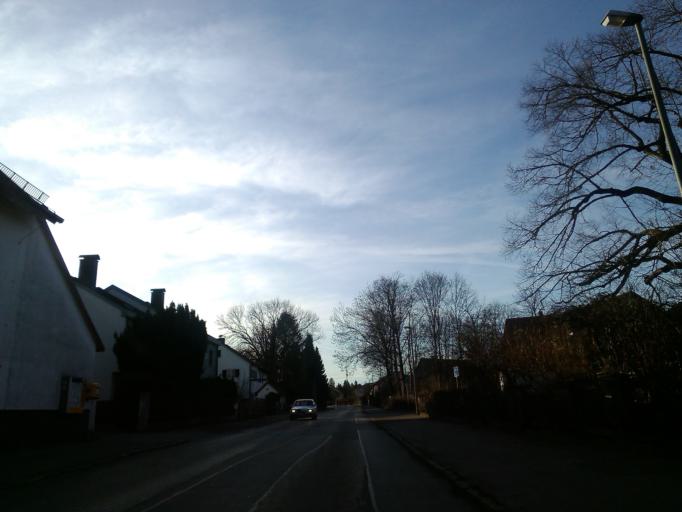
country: DE
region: Bavaria
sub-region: Upper Bavaria
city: Neuried
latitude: 48.0905
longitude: 11.4618
